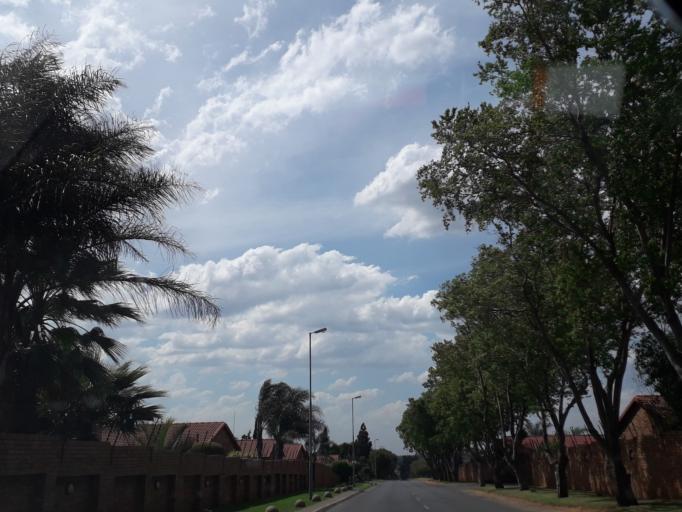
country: ZA
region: Gauteng
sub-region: City of Johannesburg Metropolitan Municipality
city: Roodepoort
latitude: -26.0976
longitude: 27.9065
